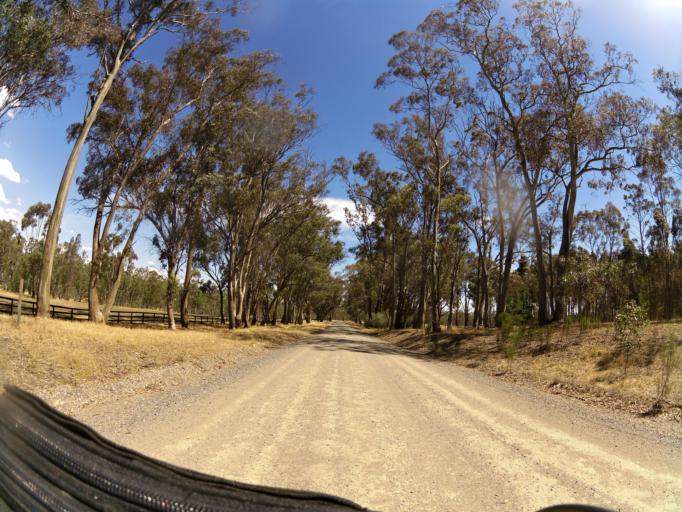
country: AU
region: Victoria
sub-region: Campaspe
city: Kyabram
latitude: -36.8255
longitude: 145.0783
